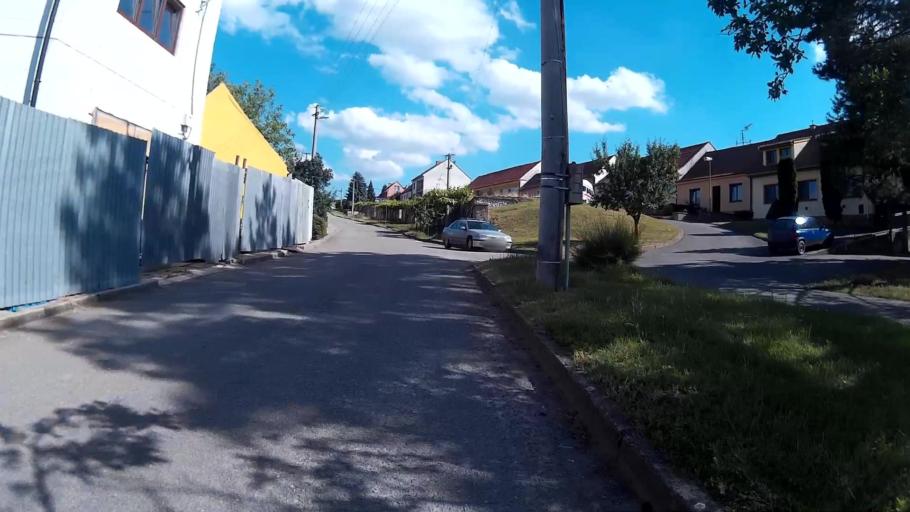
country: CZ
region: South Moravian
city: Krepice
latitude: 49.0016
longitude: 16.7178
